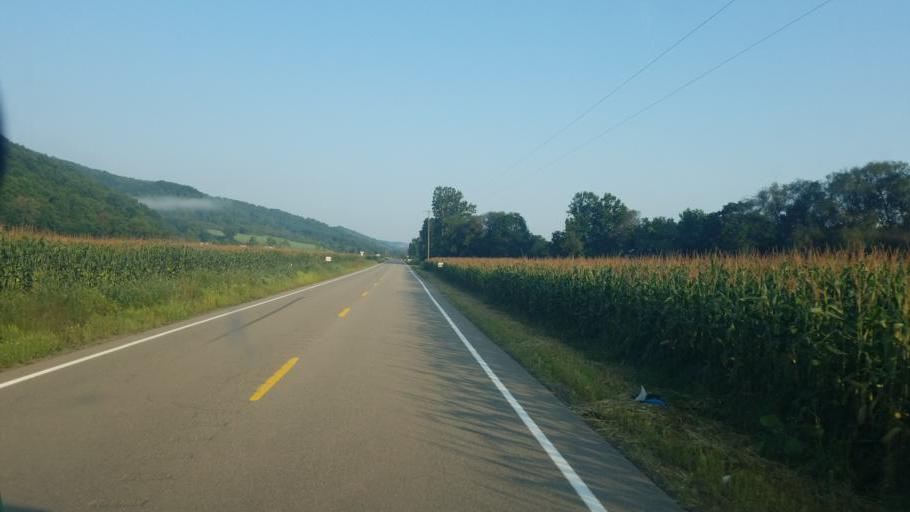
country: US
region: Pennsylvania
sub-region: Tioga County
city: Westfield
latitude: 41.9815
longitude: -77.4737
